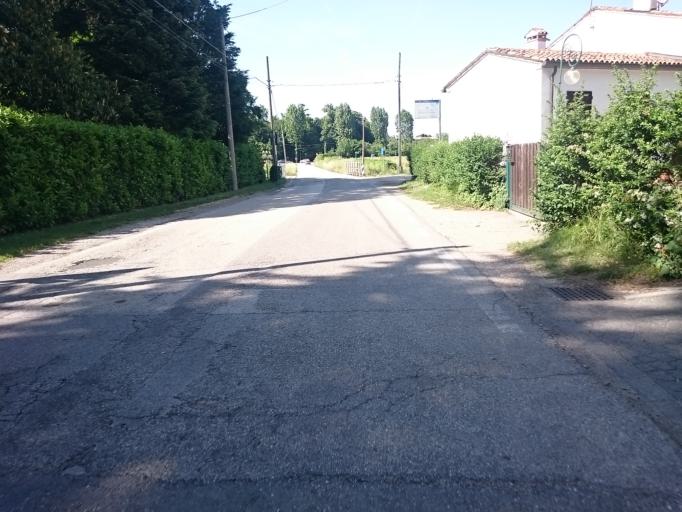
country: IT
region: Veneto
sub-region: Provincia di Padova
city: San Biagio
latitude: 45.3697
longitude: 11.7278
